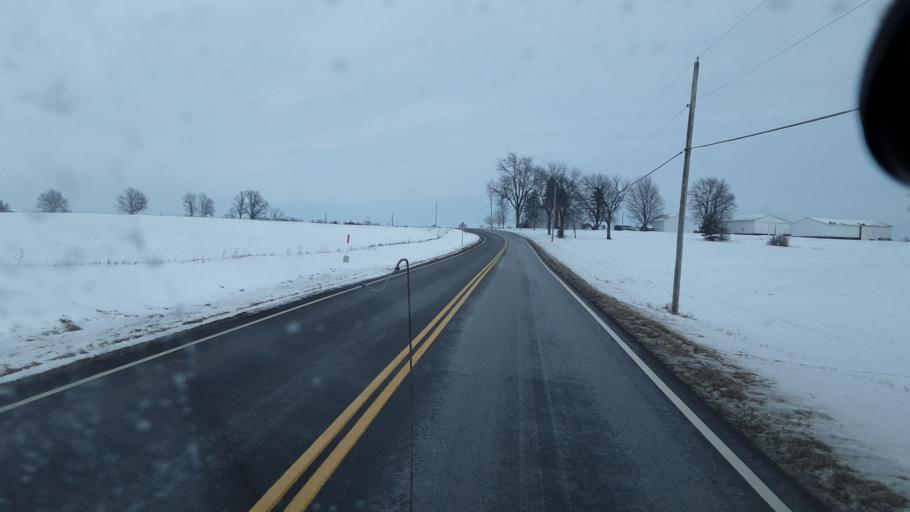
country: US
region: Ohio
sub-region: Union County
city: New California
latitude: 40.2119
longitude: -83.2612
